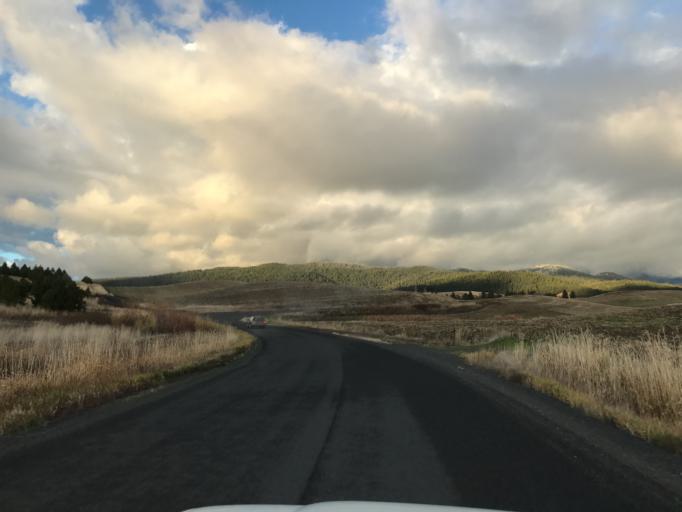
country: US
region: Idaho
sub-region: Latah County
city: Moscow
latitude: 46.7820
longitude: -116.9652
